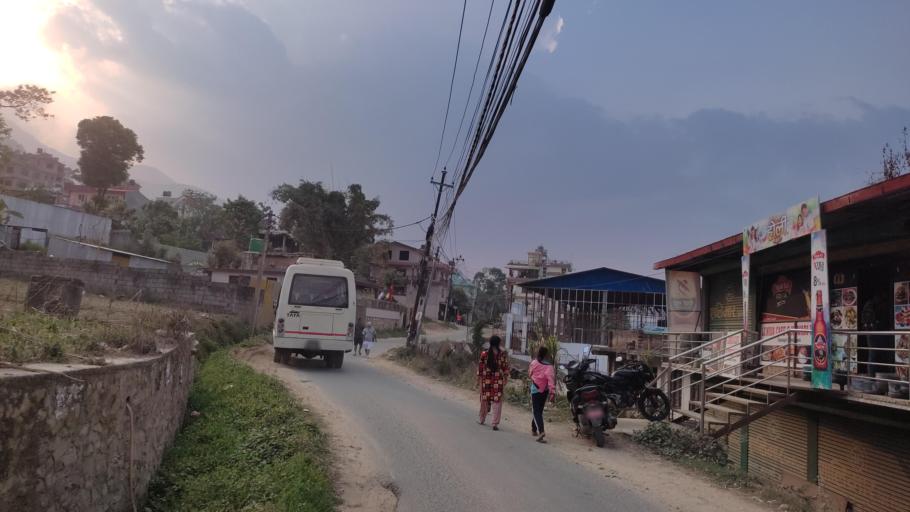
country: NP
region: Central Region
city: Kirtipur
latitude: 27.6712
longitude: 85.2482
